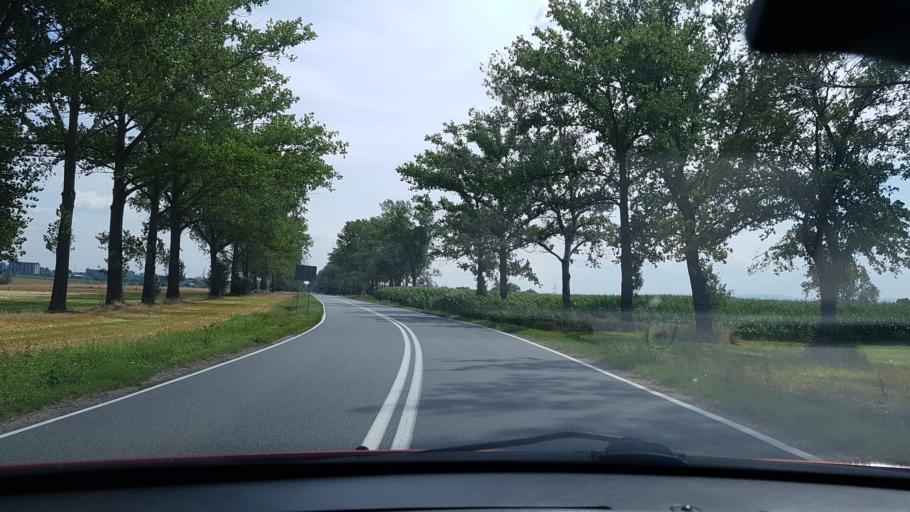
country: PL
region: Lower Silesian Voivodeship
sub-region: Powiat zabkowicki
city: Zabkowice Slaskie
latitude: 50.6082
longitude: 16.7862
